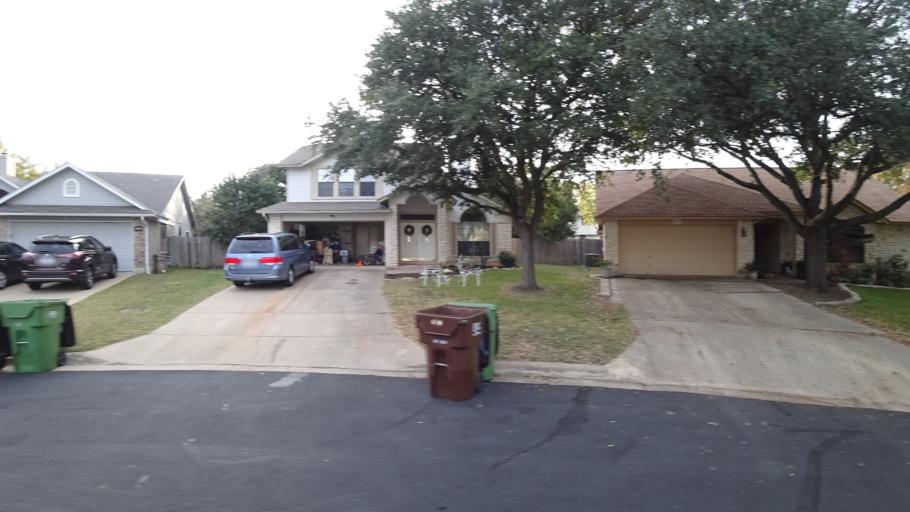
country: US
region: Texas
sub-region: Williamson County
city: Brushy Creek
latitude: 30.5153
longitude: -97.7256
